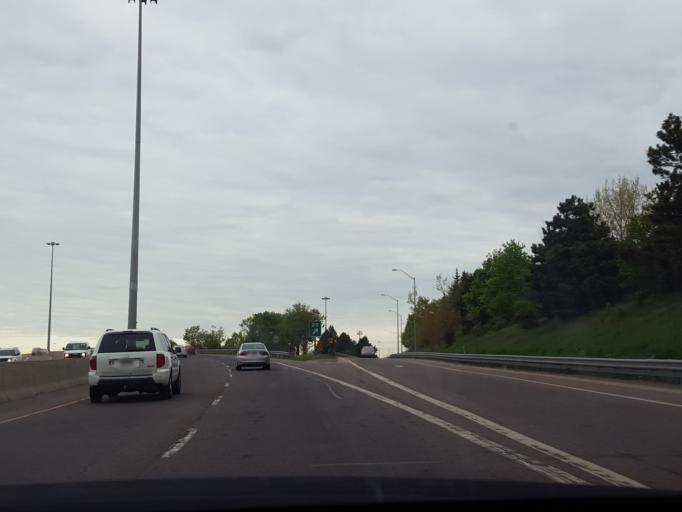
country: CA
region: Ontario
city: Toronto
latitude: 43.7102
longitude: -79.5017
